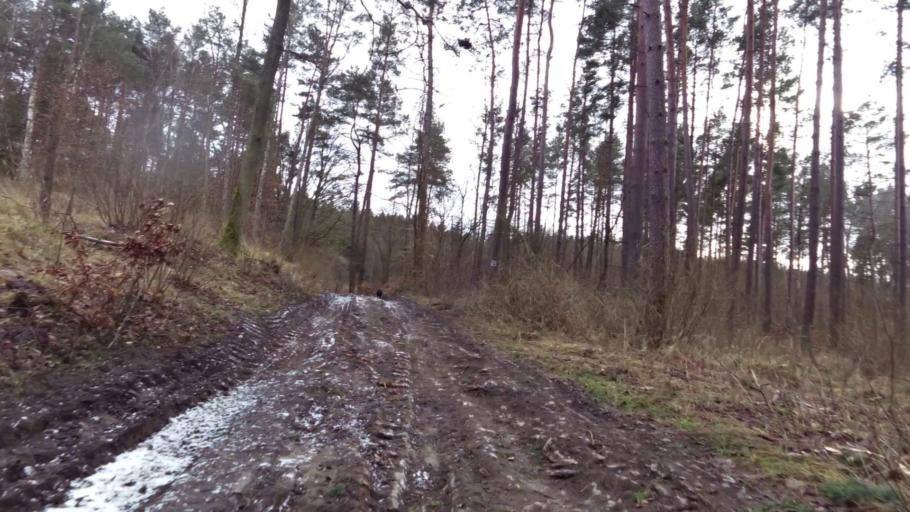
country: PL
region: West Pomeranian Voivodeship
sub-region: Powiat drawski
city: Drawsko Pomorskie
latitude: 53.5409
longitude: 15.6997
